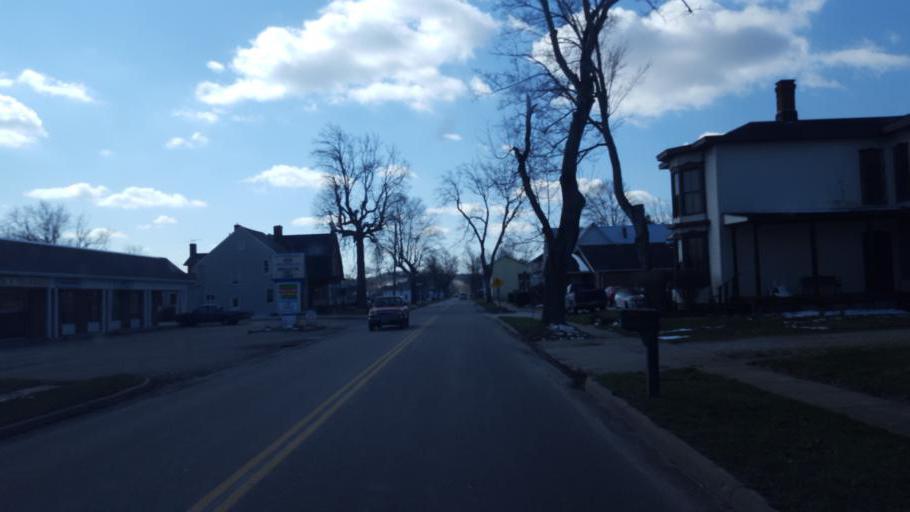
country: US
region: Ohio
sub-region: Licking County
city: Utica
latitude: 40.2380
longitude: -82.4524
